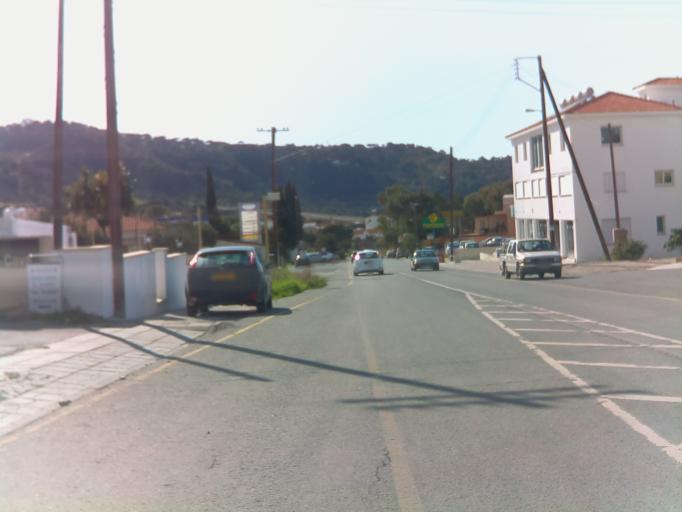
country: CY
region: Limassol
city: Pissouri
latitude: 34.6760
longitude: 32.6985
